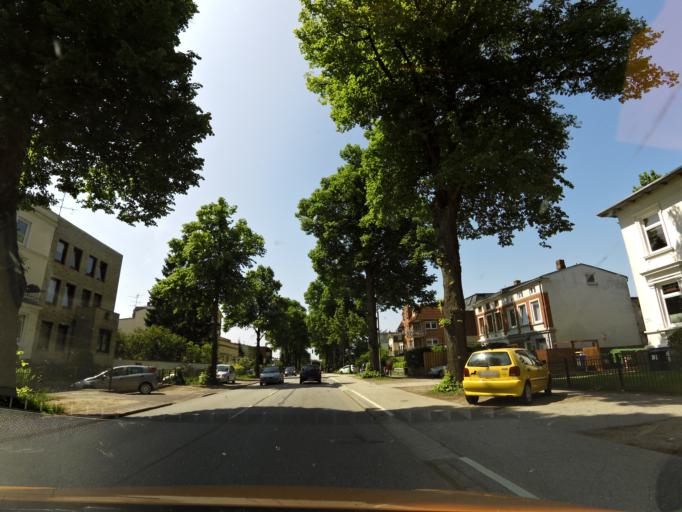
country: DE
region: Schleswig-Holstein
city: Luebeck
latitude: 53.8745
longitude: 10.7139
